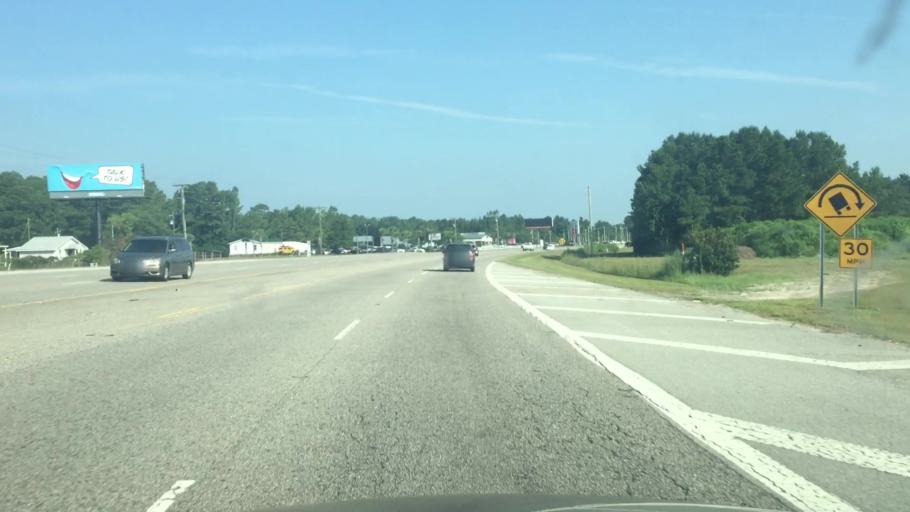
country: US
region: South Carolina
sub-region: Horry County
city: North Myrtle Beach
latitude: 33.8773
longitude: -78.6845
